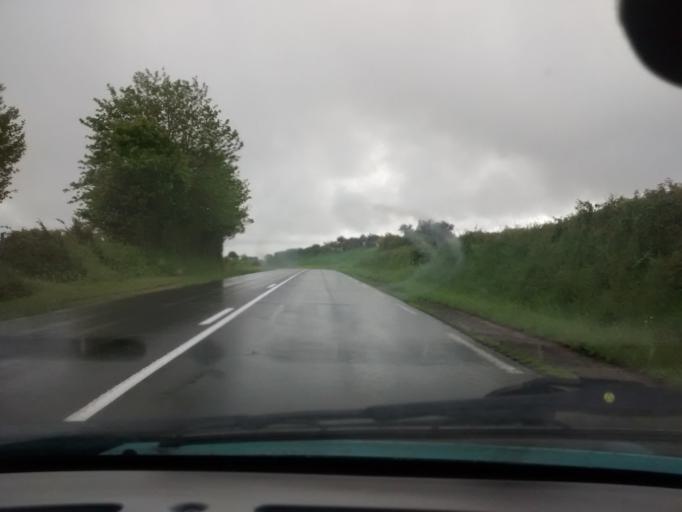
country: FR
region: Lower Normandy
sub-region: Departement de la Manche
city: Conde-sur-Vire
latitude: 49.0841
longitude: -1.0363
